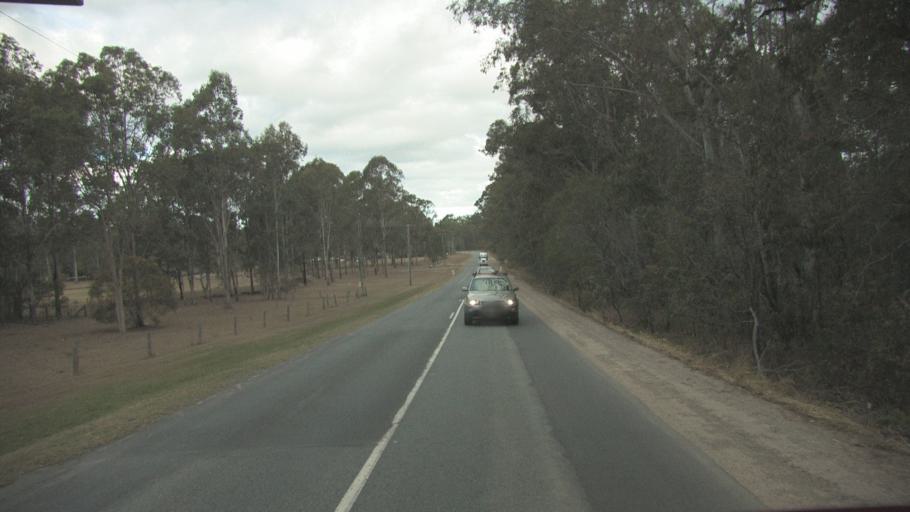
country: AU
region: Queensland
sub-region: Logan
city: Cedar Vale
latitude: -27.8582
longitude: 153.0545
